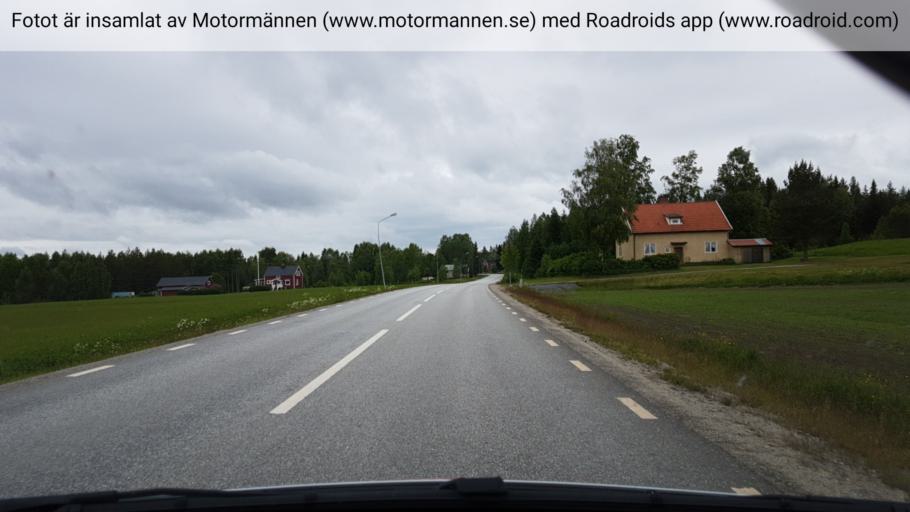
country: SE
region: Vaesterbotten
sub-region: Vindelns Kommun
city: Vindeln
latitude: 64.1073
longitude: 19.5886
